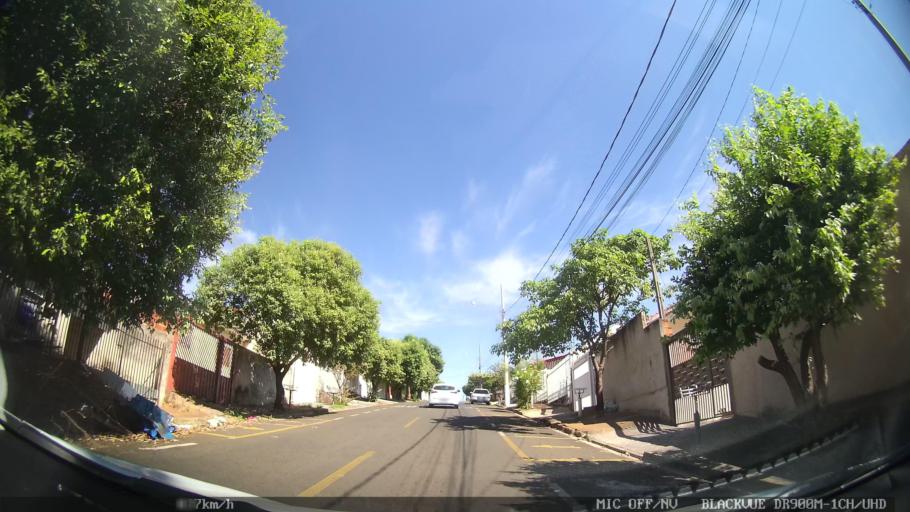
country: BR
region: Sao Paulo
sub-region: Sao Jose Do Rio Preto
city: Sao Jose do Rio Preto
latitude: -20.7749
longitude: -49.4020
